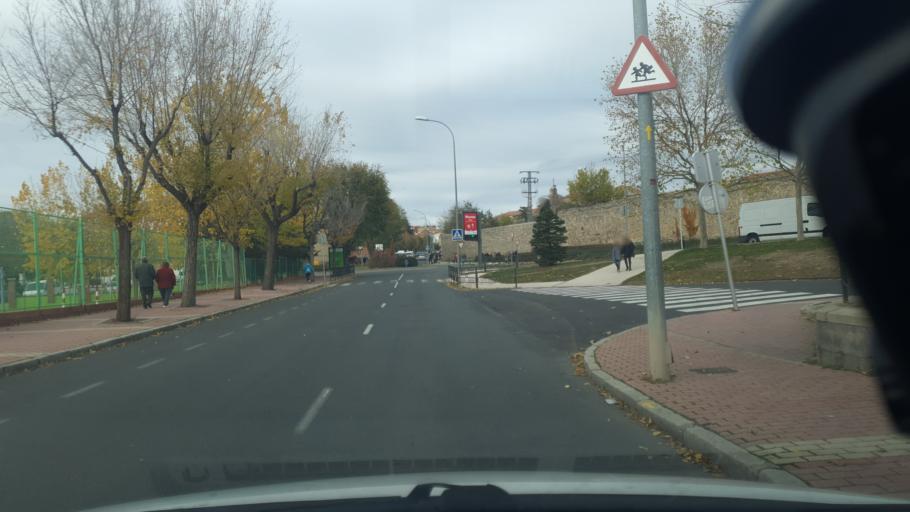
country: ES
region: Castille and Leon
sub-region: Provincia de Avila
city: Avila
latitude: 40.6479
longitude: -4.6866
